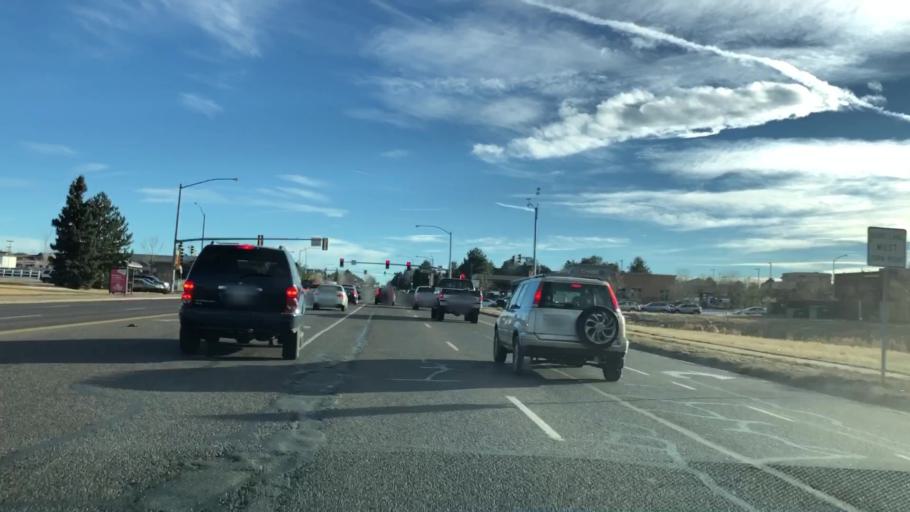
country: US
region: Colorado
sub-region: Adams County
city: Aurora
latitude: 39.6976
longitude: -104.7912
